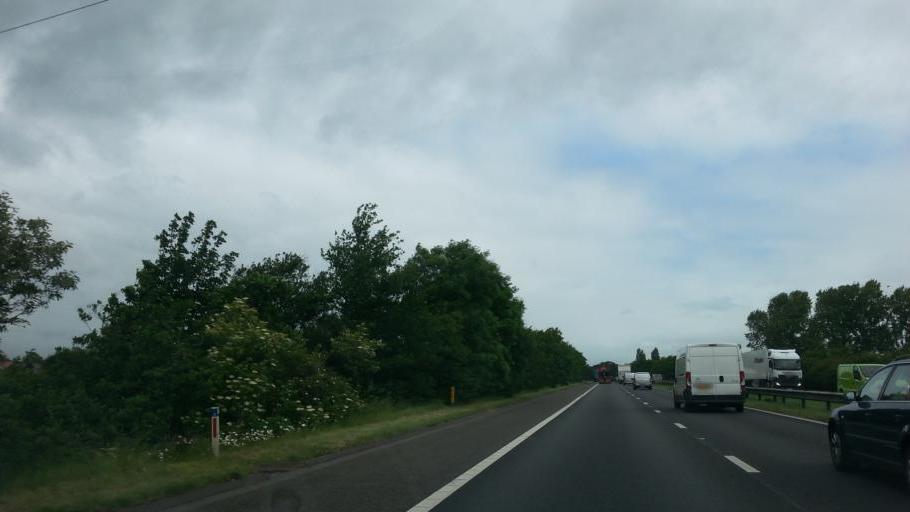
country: GB
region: England
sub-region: Doncaster
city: Tickhill
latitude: 53.4294
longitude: -1.0944
